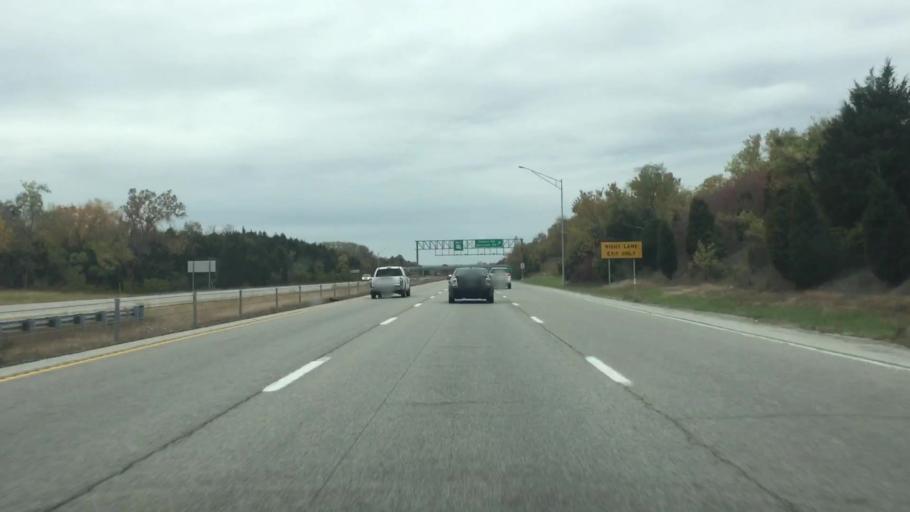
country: US
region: Missouri
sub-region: Jackson County
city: Lees Summit
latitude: 38.9384
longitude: -94.4074
